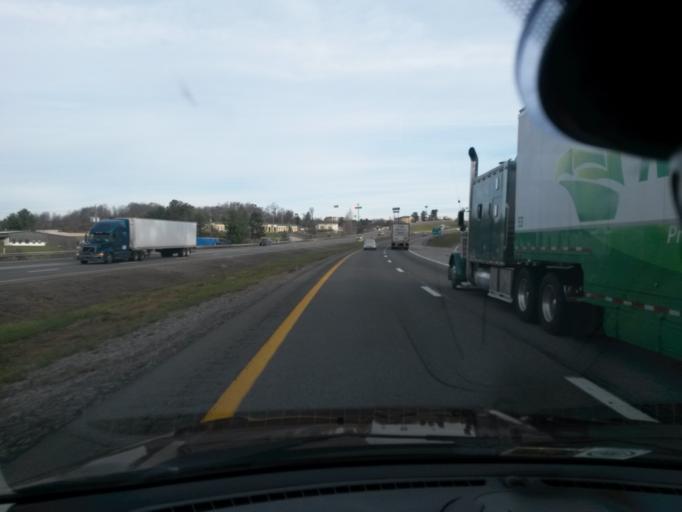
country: US
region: West Virginia
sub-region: Raleigh County
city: Mabscott
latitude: 37.7874
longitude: -81.2204
